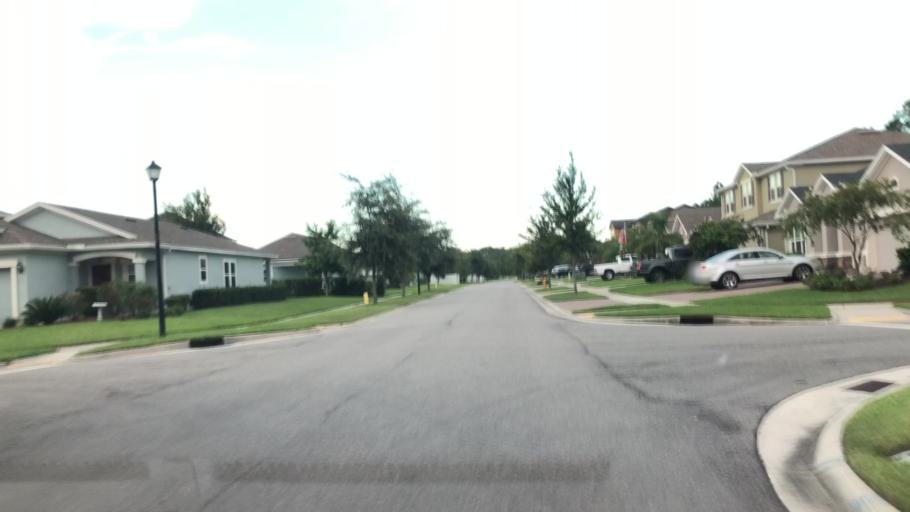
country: US
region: Florida
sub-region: Saint Johns County
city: Palm Valley
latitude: 30.0972
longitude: -81.4625
